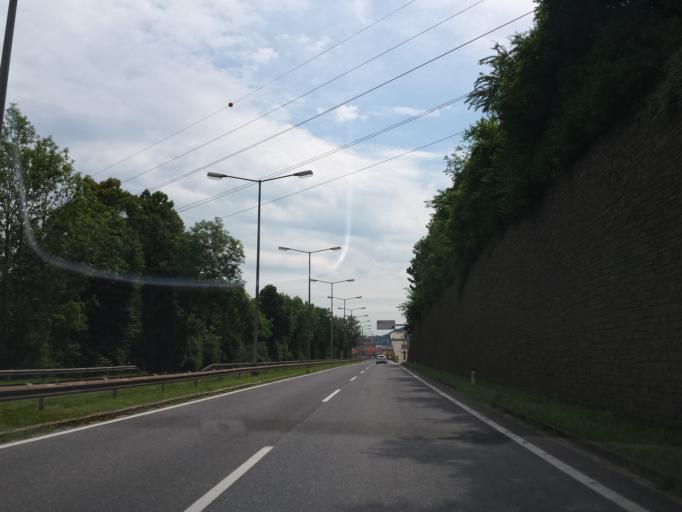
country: AT
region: Styria
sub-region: Graz Stadt
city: Goesting
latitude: 47.1063
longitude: 15.3951
